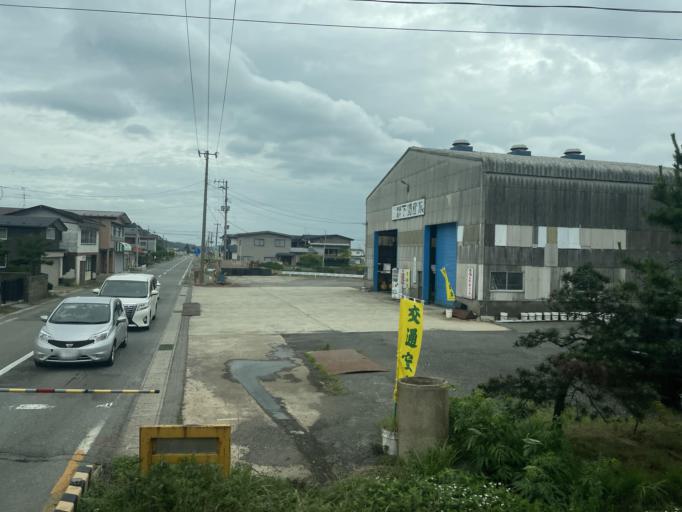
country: JP
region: Akita
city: Tenno
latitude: 39.9147
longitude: 139.9059
